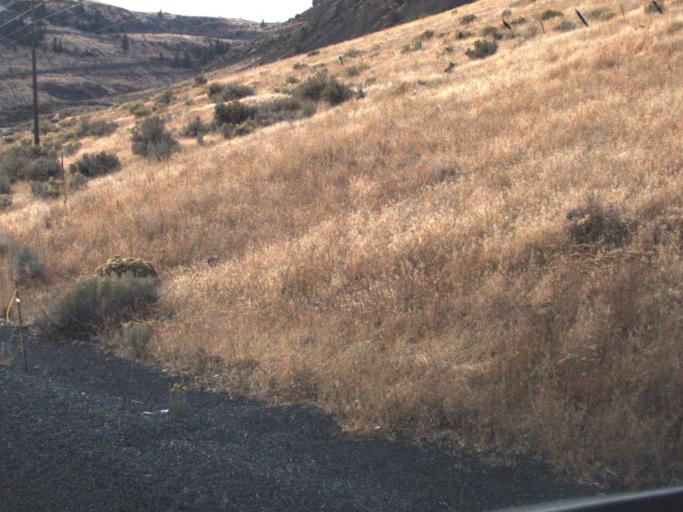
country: US
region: Washington
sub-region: Okanogan County
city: Coulee Dam
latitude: 47.9205
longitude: -118.9475
